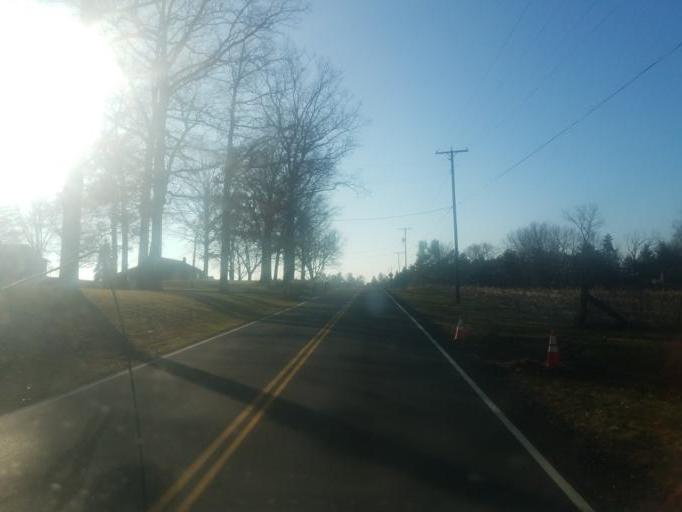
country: US
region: Ohio
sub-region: Crawford County
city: Bucyrus
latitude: 40.8211
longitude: -82.9401
